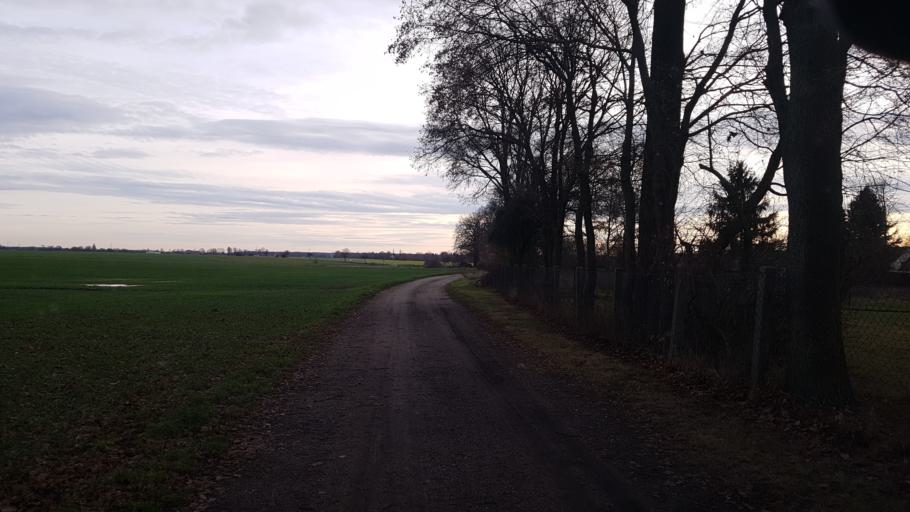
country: DE
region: Brandenburg
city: Doberlug-Kirchhain
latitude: 51.6728
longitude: 13.5127
